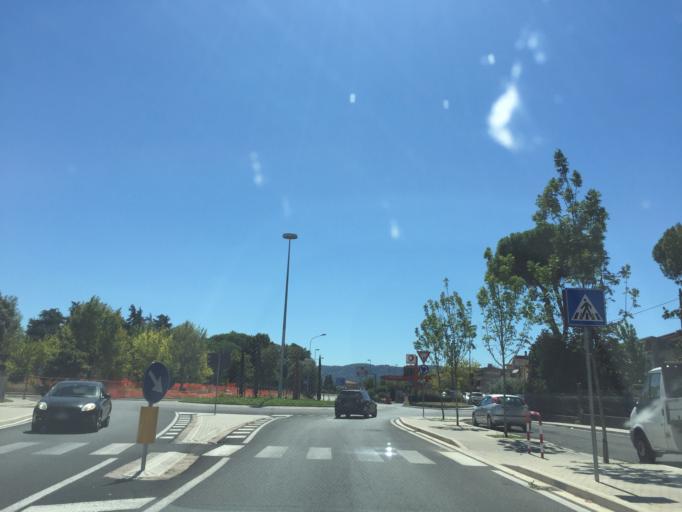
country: IT
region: Tuscany
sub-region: Provincia di Pistoia
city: Pistoia
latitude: 43.9249
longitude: 10.9184
